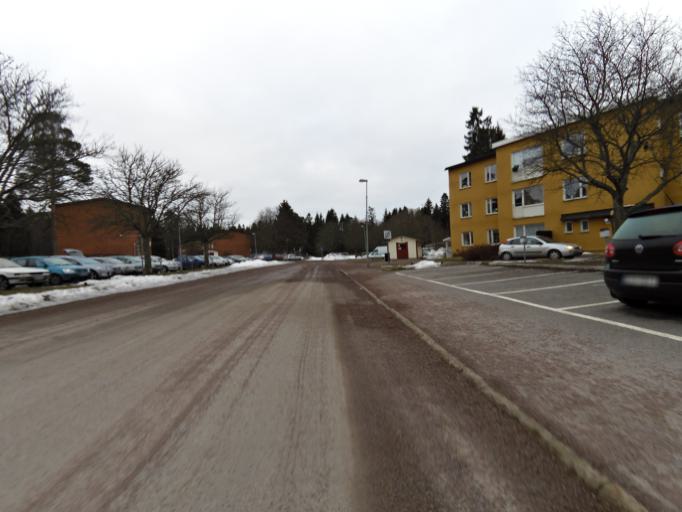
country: SE
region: Gaevleborg
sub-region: Gavle Kommun
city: Gavle
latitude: 60.6581
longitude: 17.1528
